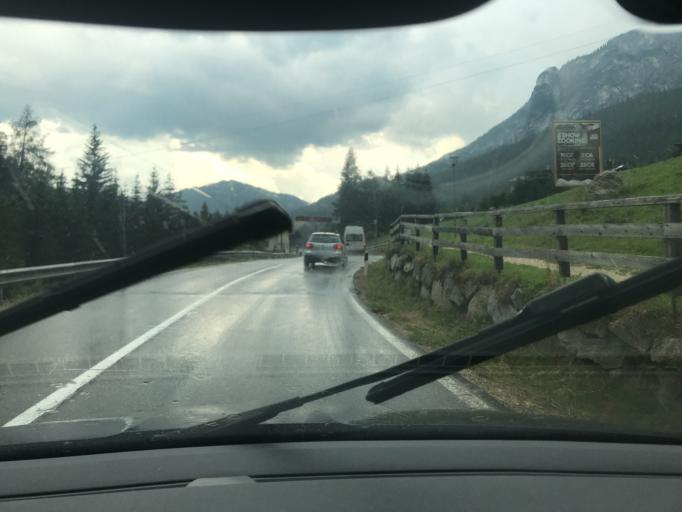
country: IT
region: Trentino-Alto Adige
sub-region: Bolzano
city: Badia
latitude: 46.6129
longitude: 11.8937
